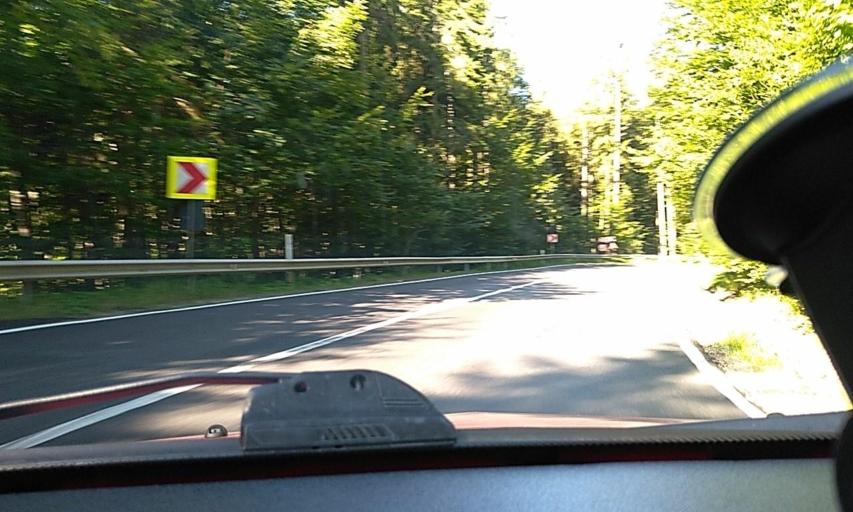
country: RO
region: Brasov
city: Crivina
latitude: 45.4936
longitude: 25.8682
